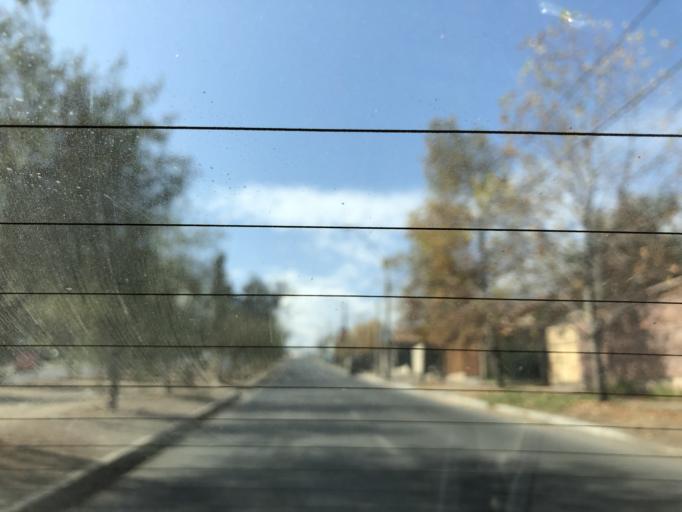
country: CL
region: Santiago Metropolitan
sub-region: Provincia de Cordillera
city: Puente Alto
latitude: -33.5753
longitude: -70.5417
